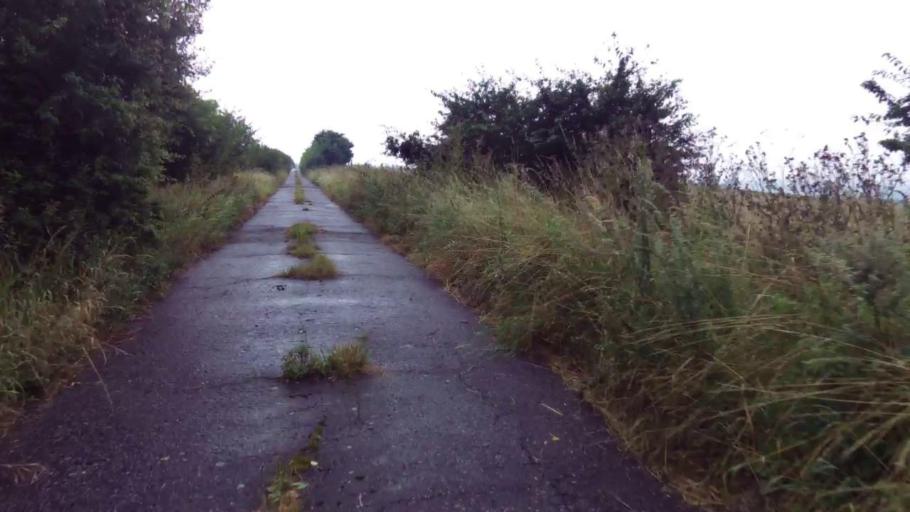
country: PL
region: West Pomeranian Voivodeship
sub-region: Powiat choszczenski
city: Recz
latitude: 53.2515
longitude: 15.4627
